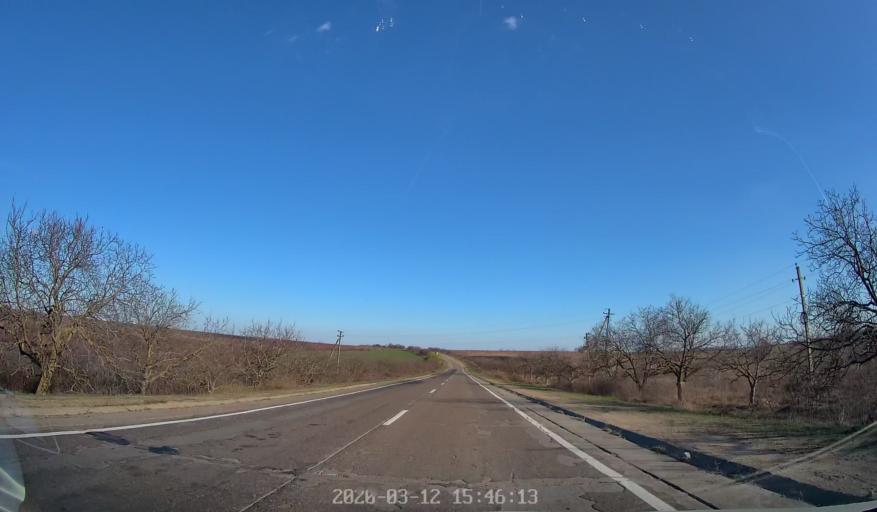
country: MD
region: Chisinau
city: Stauceni
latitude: 47.1009
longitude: 28.8887
